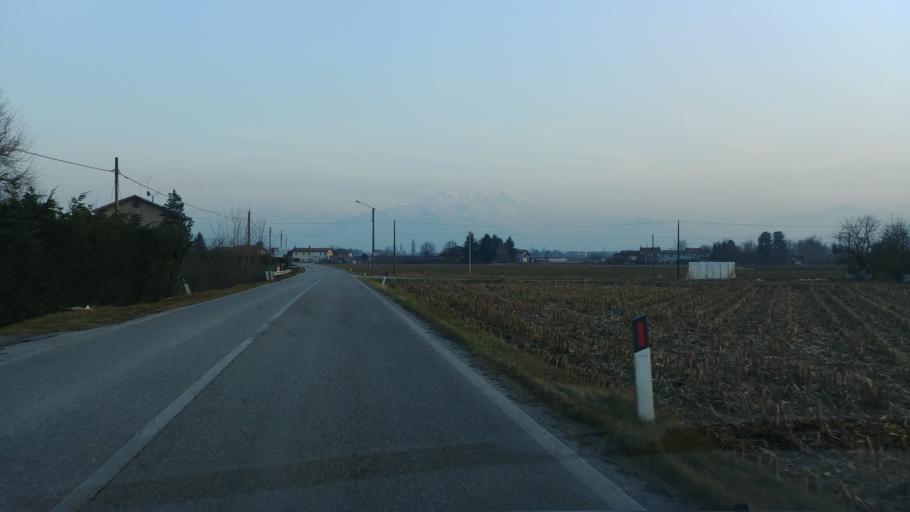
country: IT
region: Piedmont
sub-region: Provincia di Cuneo
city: Roata Rossi
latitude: 44.4158
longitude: 7.5112
